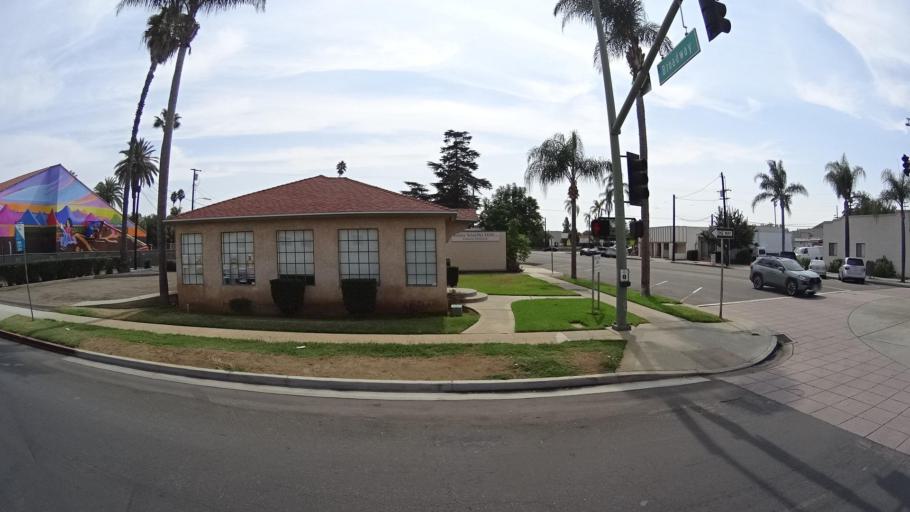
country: US
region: California
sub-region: San Diego County
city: Escondido
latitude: 33.1207
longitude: -117.0808
